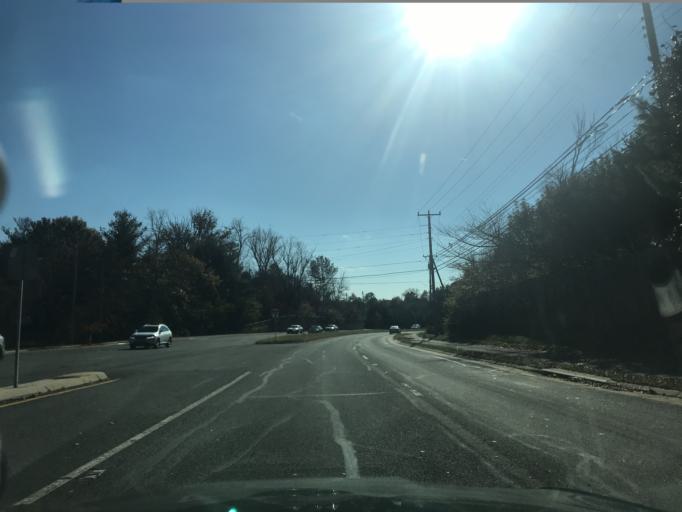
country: US
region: Virginia
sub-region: Fairfax County
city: Oak Hill
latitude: 38.9084
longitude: -77.3810
